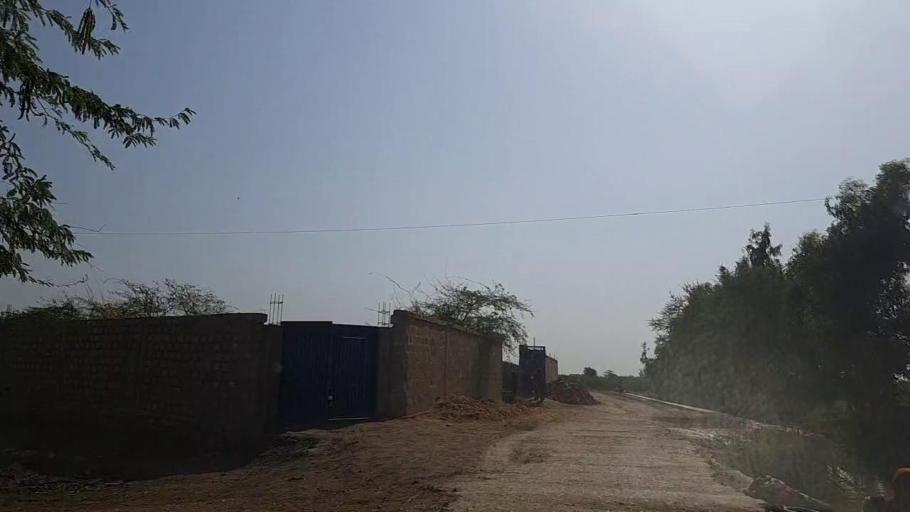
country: PK
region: Sindh
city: Daro Mehar
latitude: 24.7192
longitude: 68.0789
